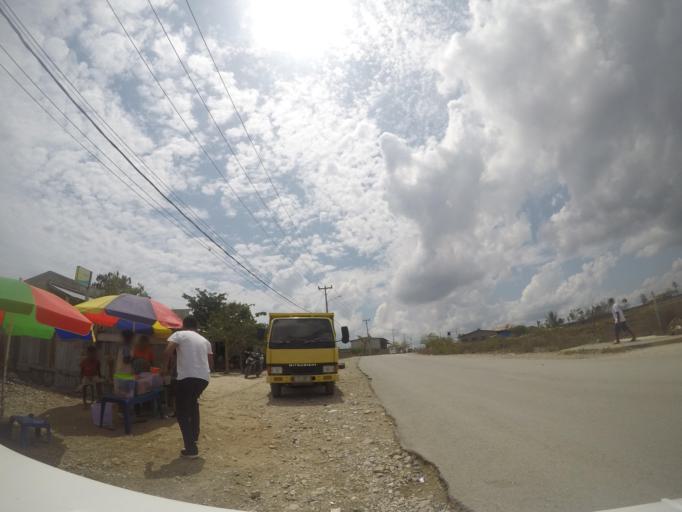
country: TL
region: Baucau
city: Baucau
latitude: -8.4763
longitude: 126.4495
